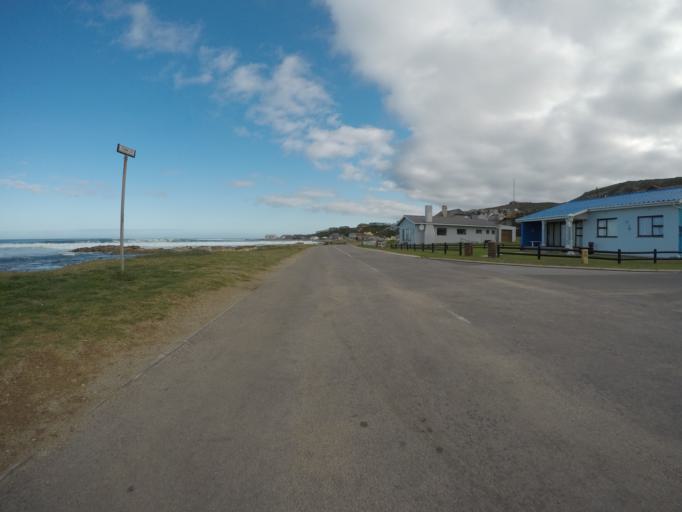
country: ZA
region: Western Cape
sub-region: Eden District Municipality
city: Riversdale
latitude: -34.4272
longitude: 21.3376
